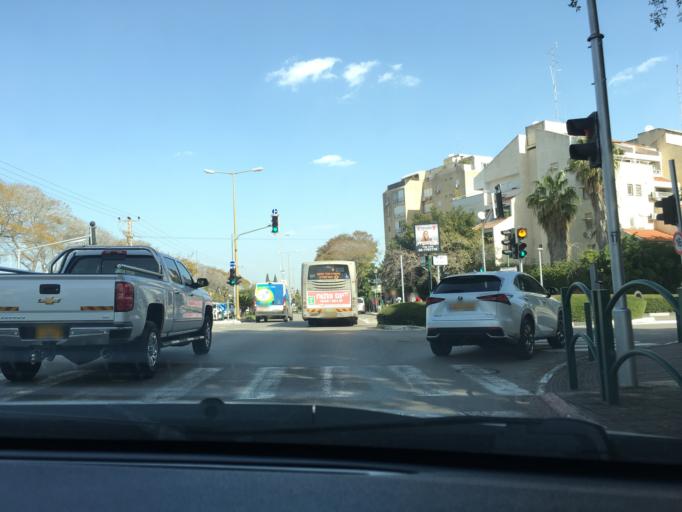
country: IL
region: Central District
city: Kfar Saba
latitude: 32.1805
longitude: 34.8972
